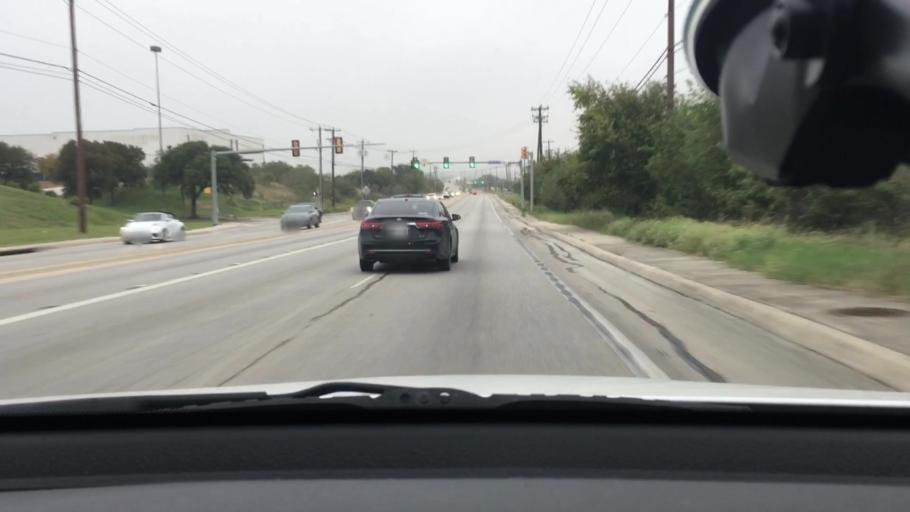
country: US
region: Texas
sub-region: Bexar County
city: Live Oak
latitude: 29.5935
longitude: -98.3482
